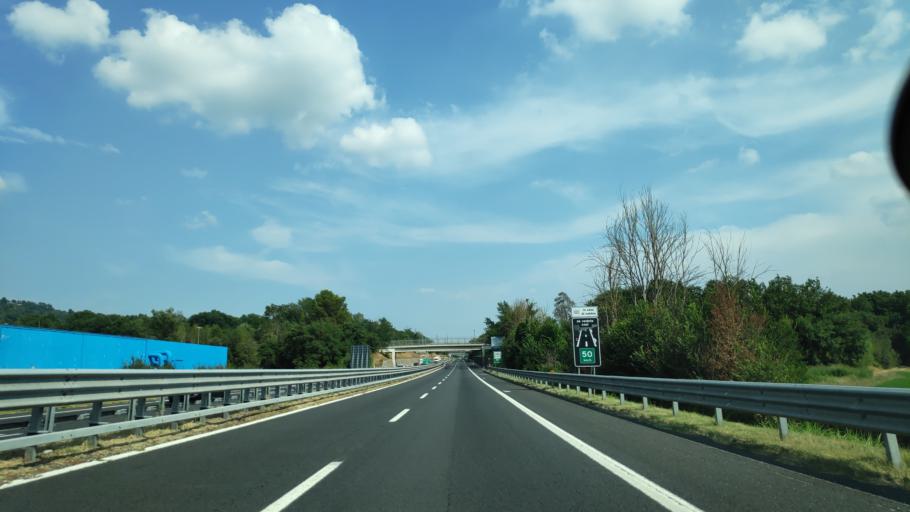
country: IT
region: Umbria
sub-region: Provincia di Terni
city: Attigliano
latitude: 42.5057
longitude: 12.3006
